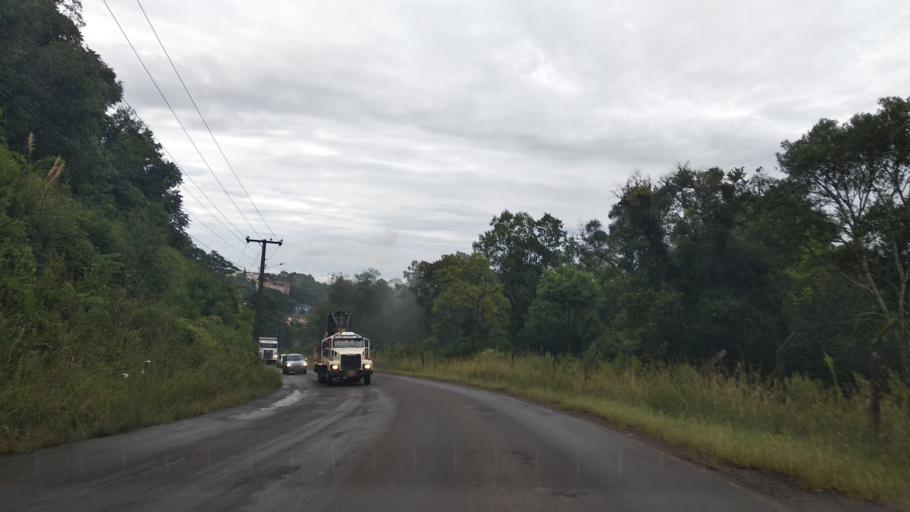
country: BR
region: Santa Catarina
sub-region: Videira
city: Videira
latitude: -26.9967
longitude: -51.1800
